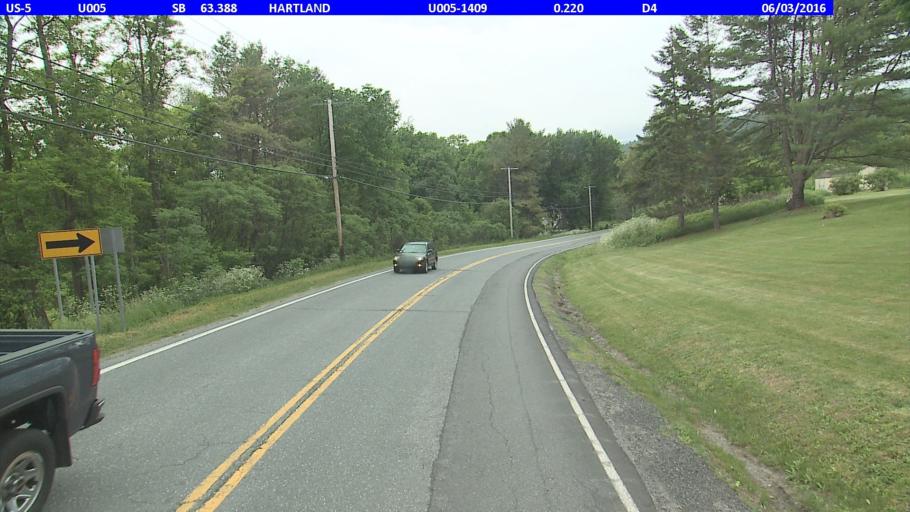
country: US
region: Vermont
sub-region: Windsor County
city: Windsor
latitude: 43.5231
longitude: -72.3993
